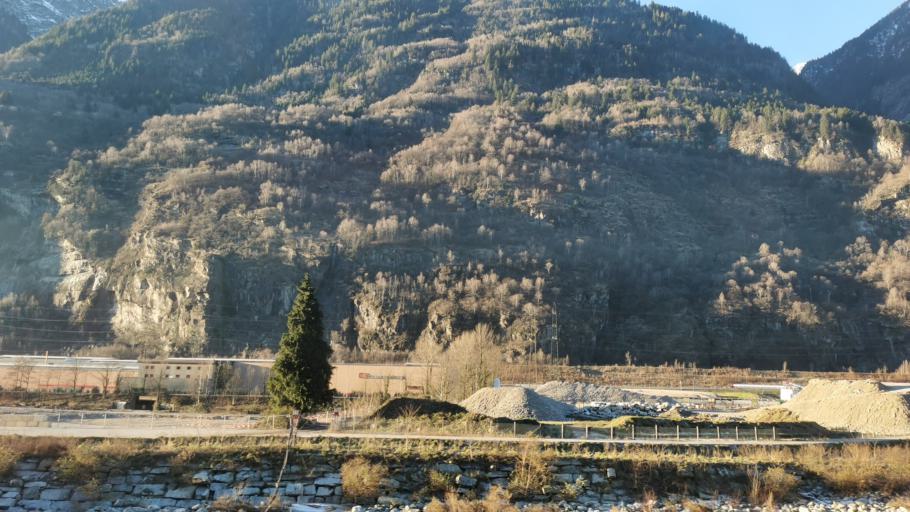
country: CH
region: Ticino
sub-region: Leventina District
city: Bodio
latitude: 46.3911
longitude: 8.8926
